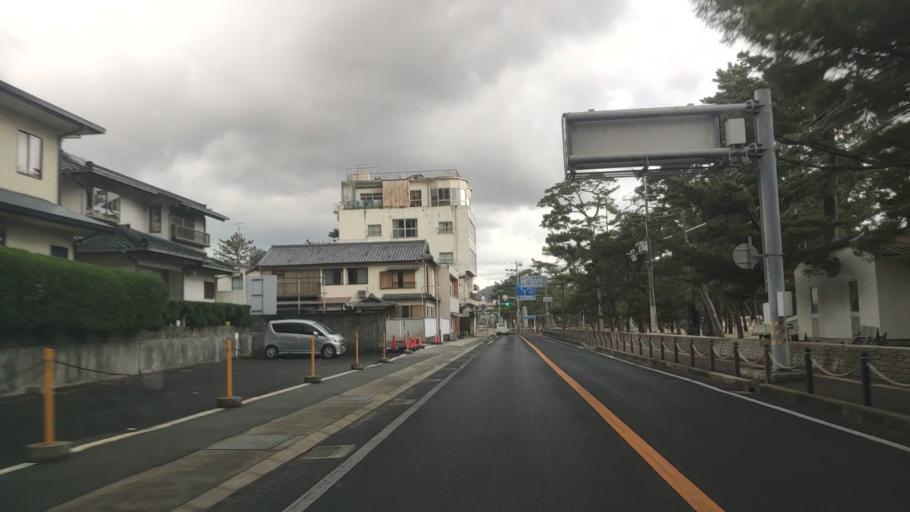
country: JP
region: Hyogo
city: Sumoto
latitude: 34.3403
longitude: 134.9033
